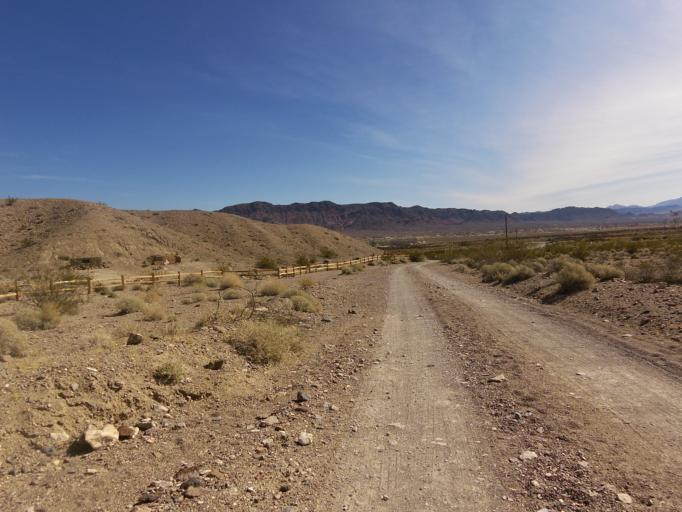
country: US
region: Nevada
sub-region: Nye County
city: Pahrump
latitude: 35.9734
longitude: -116.2727
